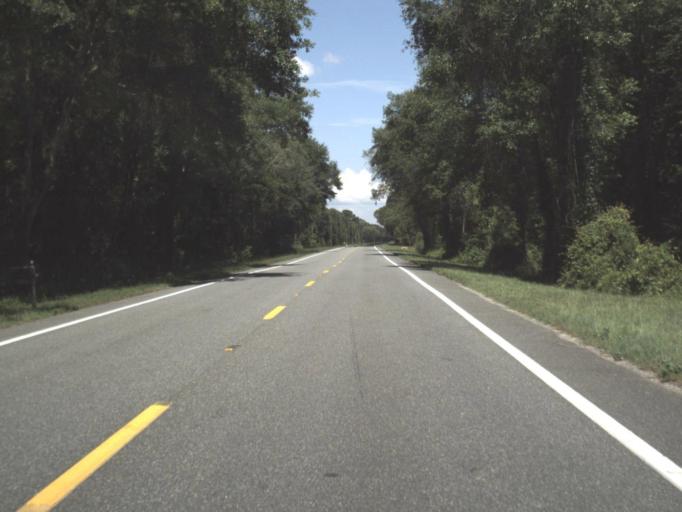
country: US
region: Florida
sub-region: Lafayette County
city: Mayo
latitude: 30.1294
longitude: -83.3327
